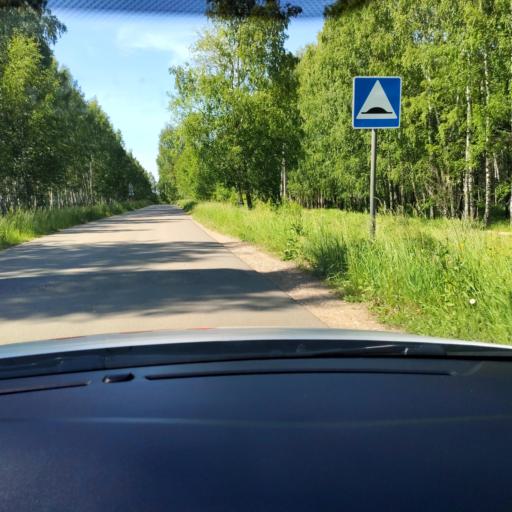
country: RU
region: Tatarstan
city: Staroye Arakchino
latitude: 55.8875
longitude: 49.0361
